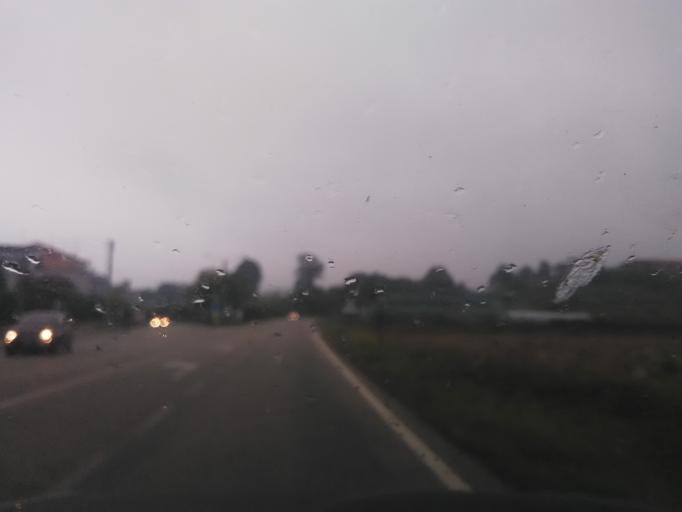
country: IT
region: Piedmont
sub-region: Provincia di Biella
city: Cavaglia
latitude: 45.4057
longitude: 8.0987
